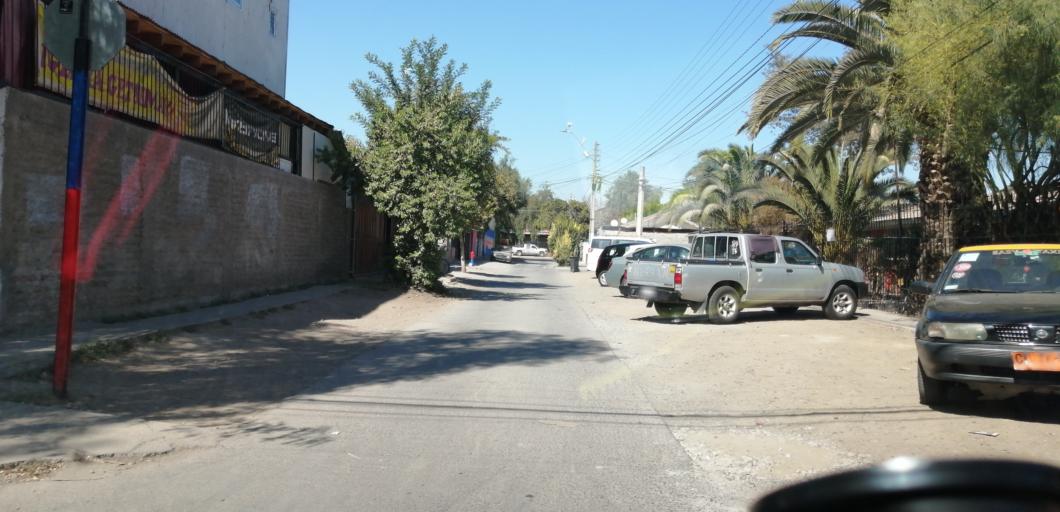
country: CL
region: Santiago Metropolitan
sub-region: Provincia de Santiago
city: Lo Prado
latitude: -33.4330
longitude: -70.7610
